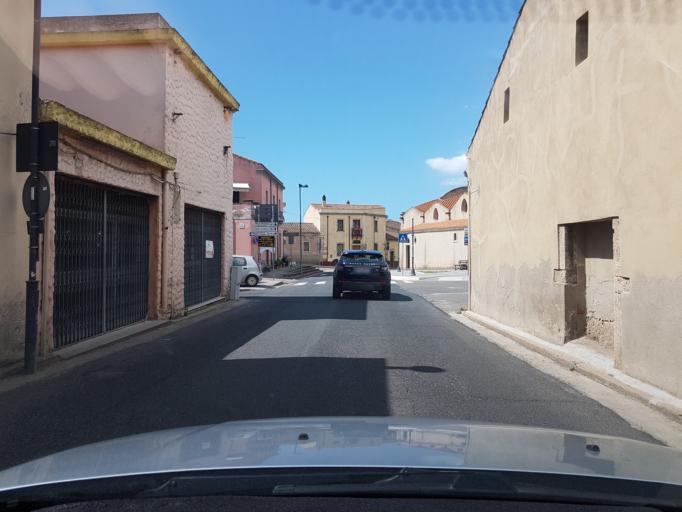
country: IT
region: Sardinia
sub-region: Provincia di Oristano
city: Riola Sardo
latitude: 39.9951
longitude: 8.5398
